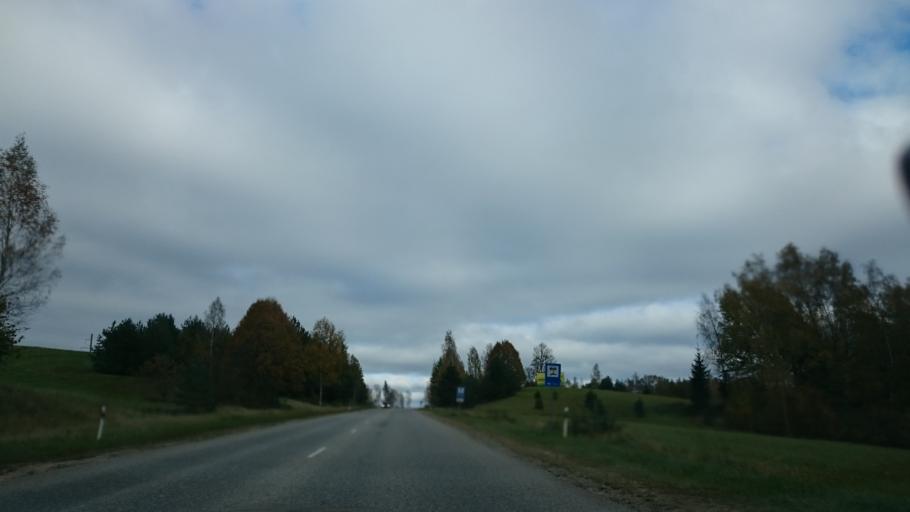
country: LV
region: Amatas Novads
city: Drabesi
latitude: 57.2649
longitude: 25.2710
